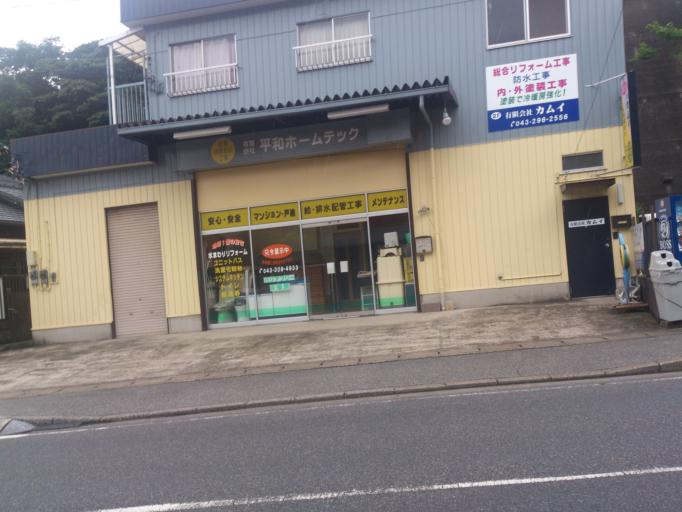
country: JP
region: Chiba
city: Chiba
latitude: 35.6424
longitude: 140.0724
